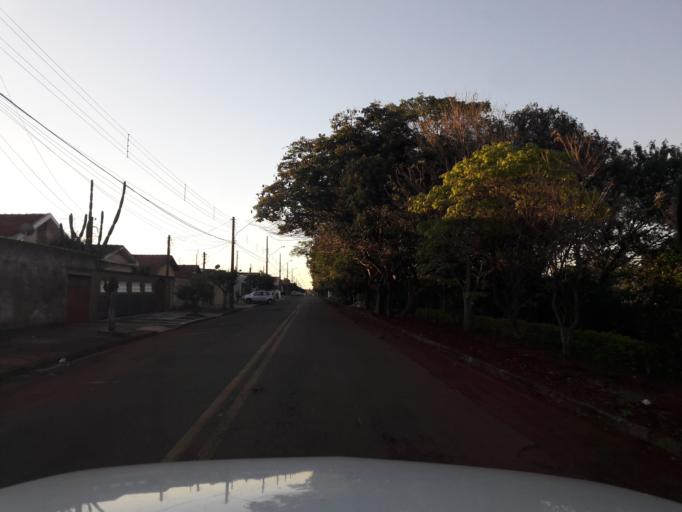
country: BR
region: Sao Paulo
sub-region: Moji-Guacu
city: Mogi-Gaucu
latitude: -22.3486
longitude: -46.9338
